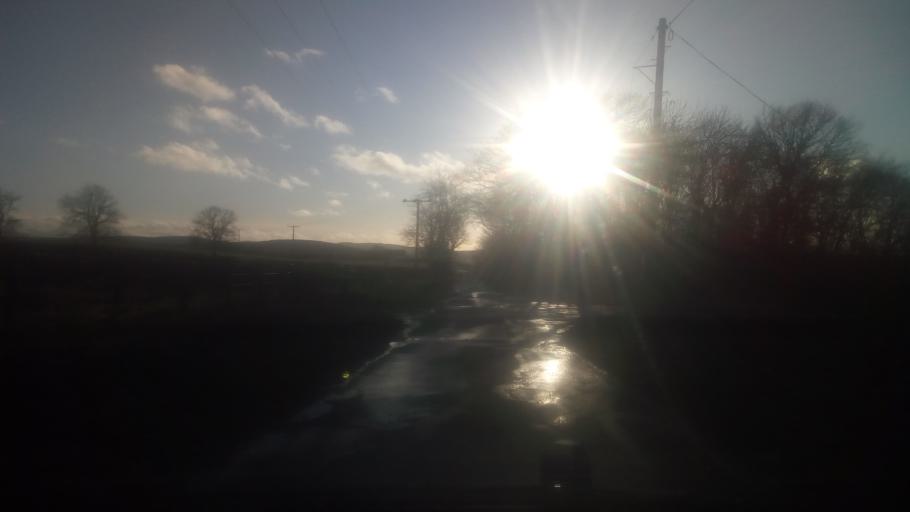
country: GB
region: Scotland
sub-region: The Scottish Borders
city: Jedburgh
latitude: 55.4699
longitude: -2.4606
